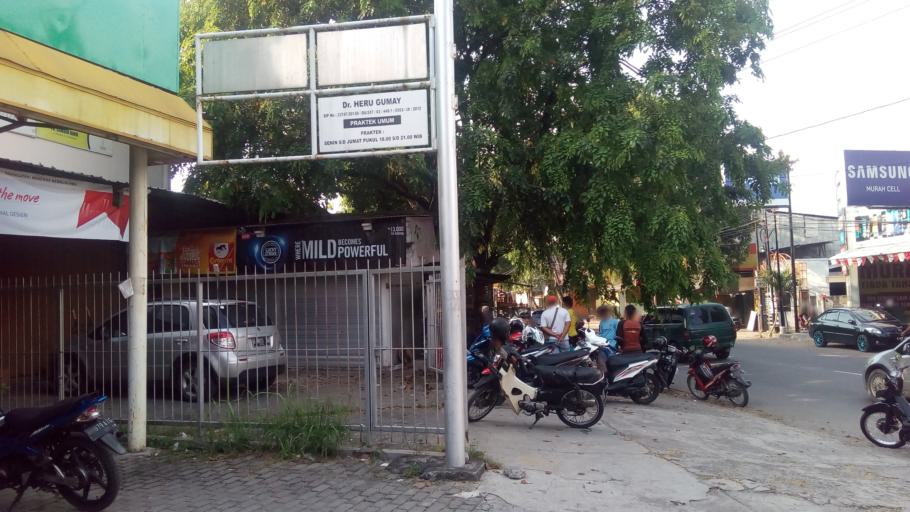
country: ID
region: Central Java
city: Mranggen
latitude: -7.0162
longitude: 110.4720
